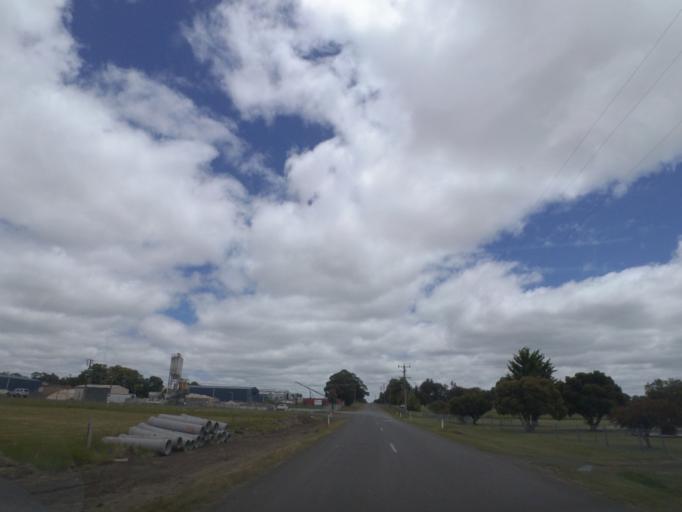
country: AU
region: Victoria
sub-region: Moorabool
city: Bacchus Marsh
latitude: -37.6095
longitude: 144.2396
